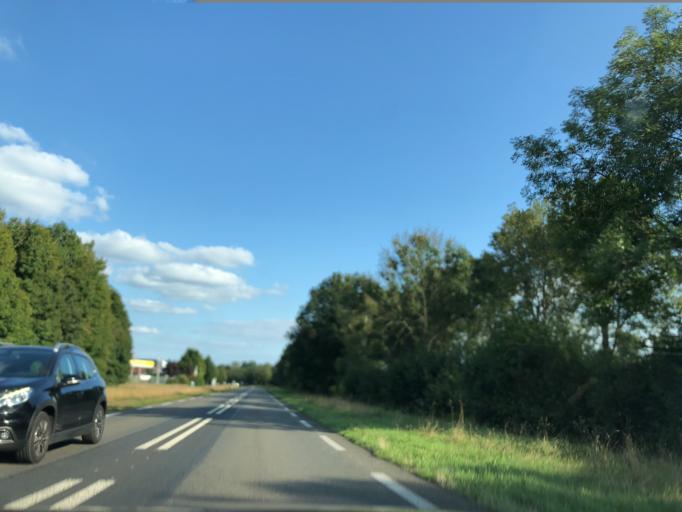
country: NL
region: Groningen
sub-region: Gemeente Stadskanaal
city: Stadskanaal
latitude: 52.9765
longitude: 6.9475
